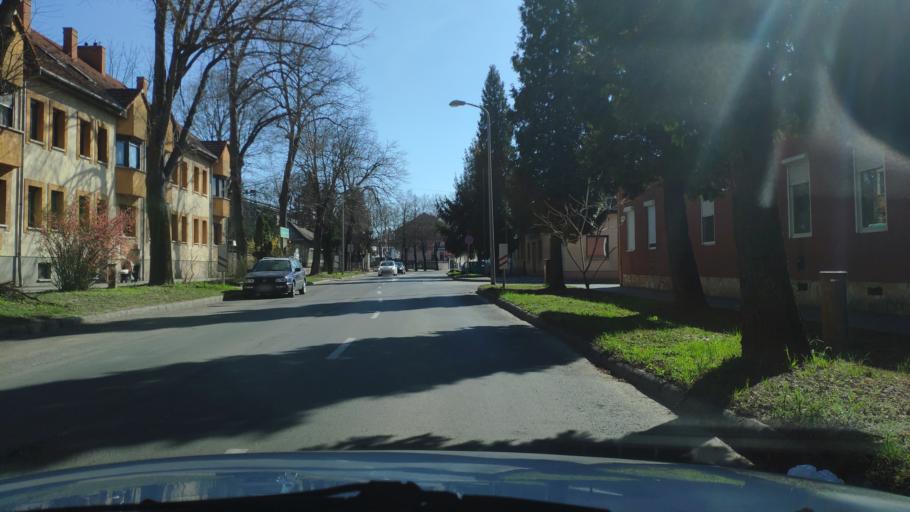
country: HU
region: Zala
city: Nagykanizsa
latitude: 46.4497
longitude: 16.9916
